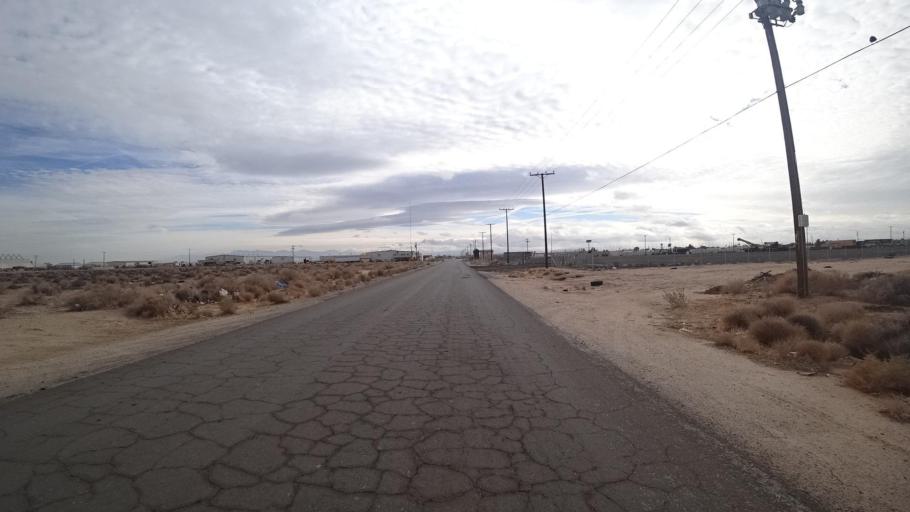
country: US
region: California
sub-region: Kern County
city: Rosamond
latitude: 34.8590
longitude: -118.1584
